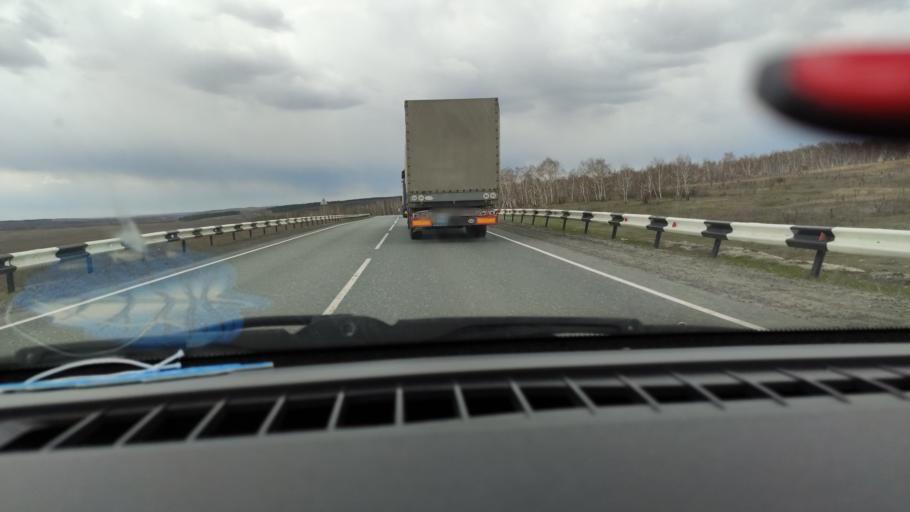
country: RU
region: Saratov
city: Sennoy
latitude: 52.1325
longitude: 46.8642
